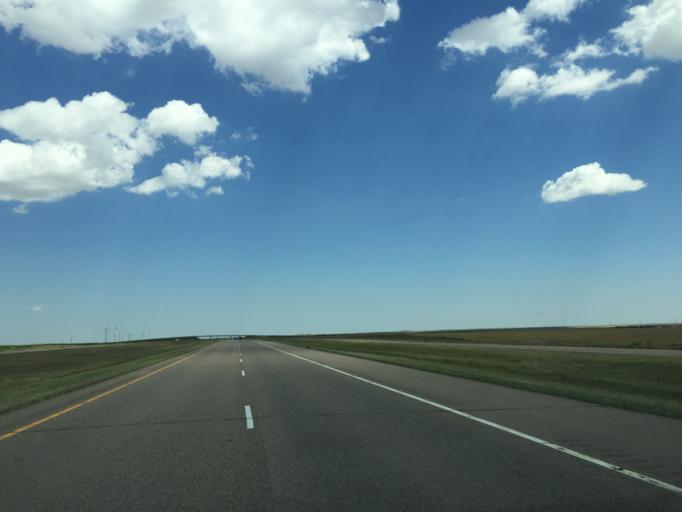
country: US
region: Colorado
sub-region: Lincoln County
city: Hugo
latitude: 39.2774
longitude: -103.4531
